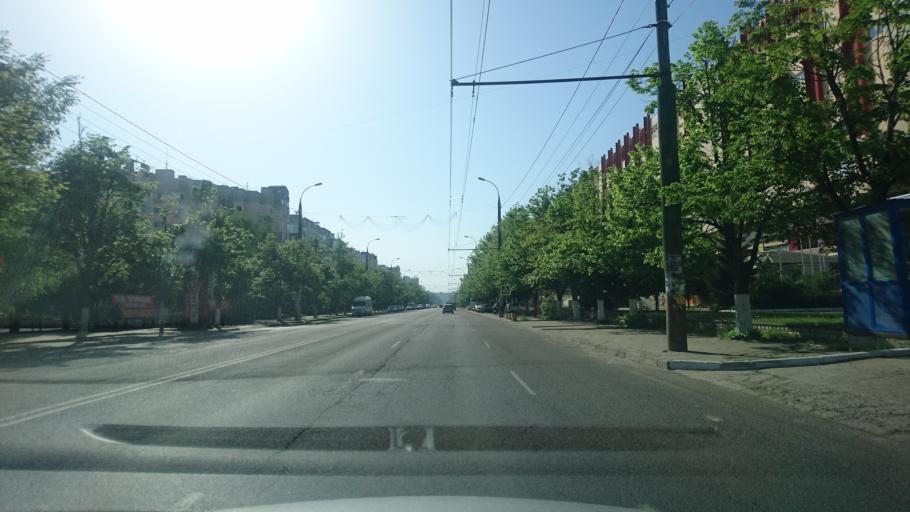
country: MD
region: Chisinau
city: Vatra
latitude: 47.0373
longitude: 28.7717
